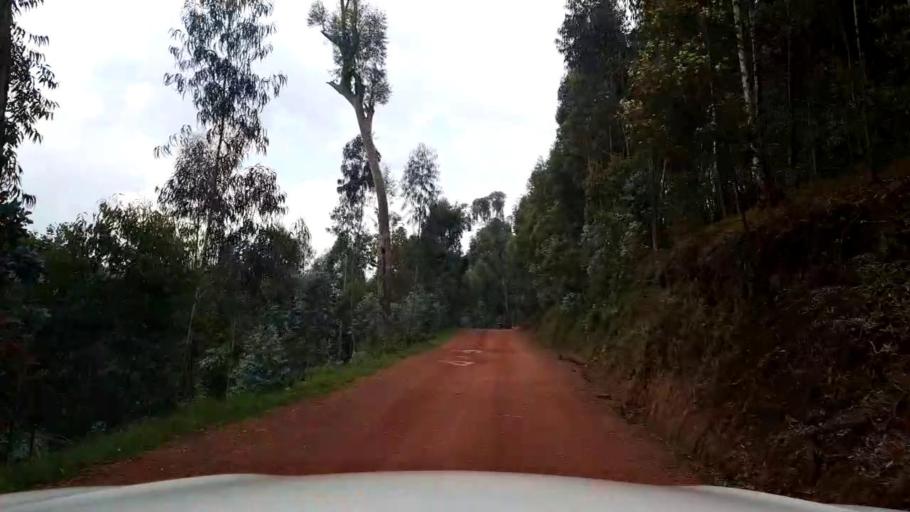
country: RW
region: Northern Province
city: Byumba
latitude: -1.5228
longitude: 29.9522
